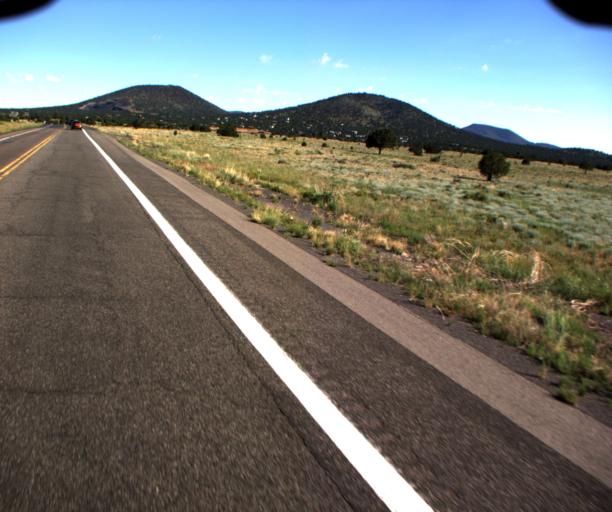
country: US
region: Arizona
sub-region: Coconino County
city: Williams
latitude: 35.3137
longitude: -112.1478
